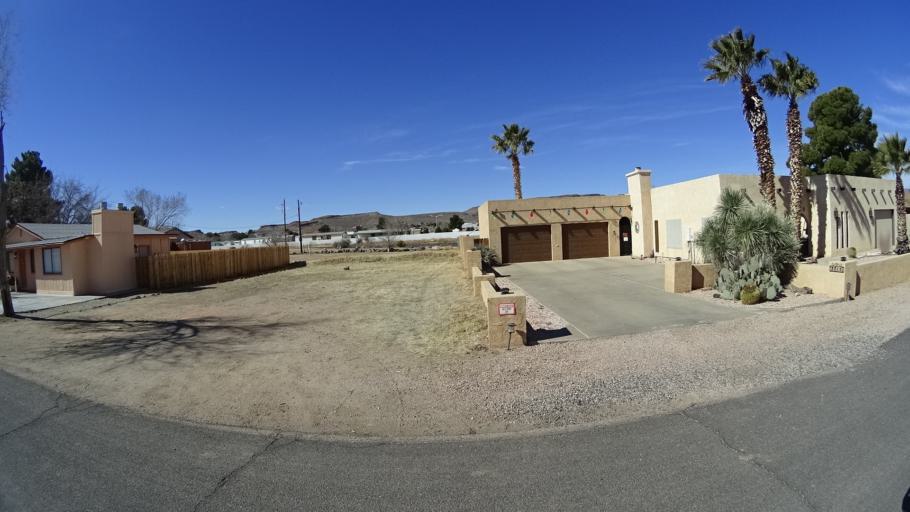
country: US
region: Arizona
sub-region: Mohave County
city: New Kingman-Butler
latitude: 35.2310
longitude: -114.0283
